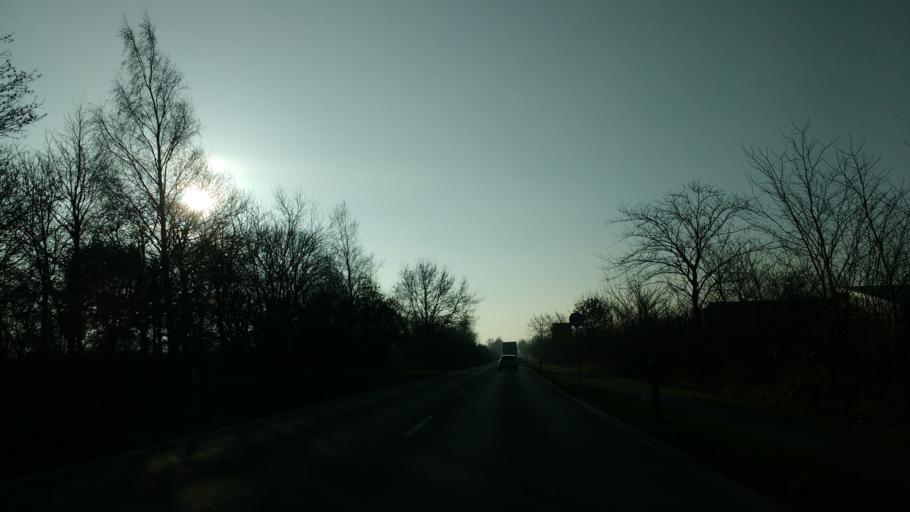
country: DE
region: Schleswig-Holstein
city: Poschendorf
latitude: 54.0391
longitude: 9.4806
